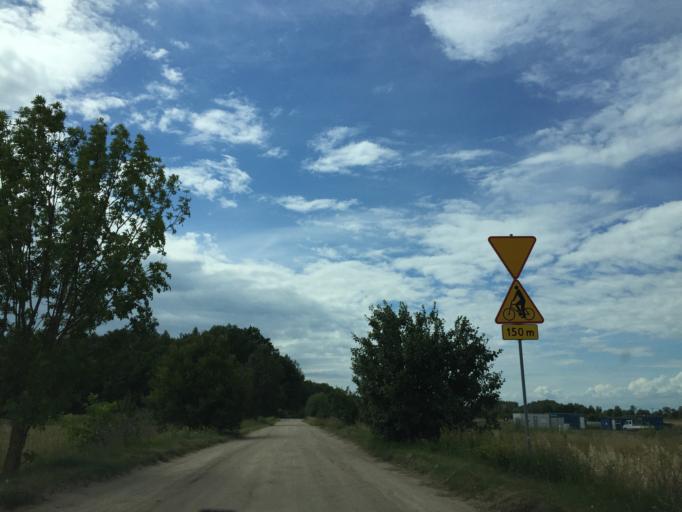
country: PL
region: Podlasie
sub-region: Powiat bielski
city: Bielsk Podlaski
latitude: 52.7446
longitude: 23.1829
